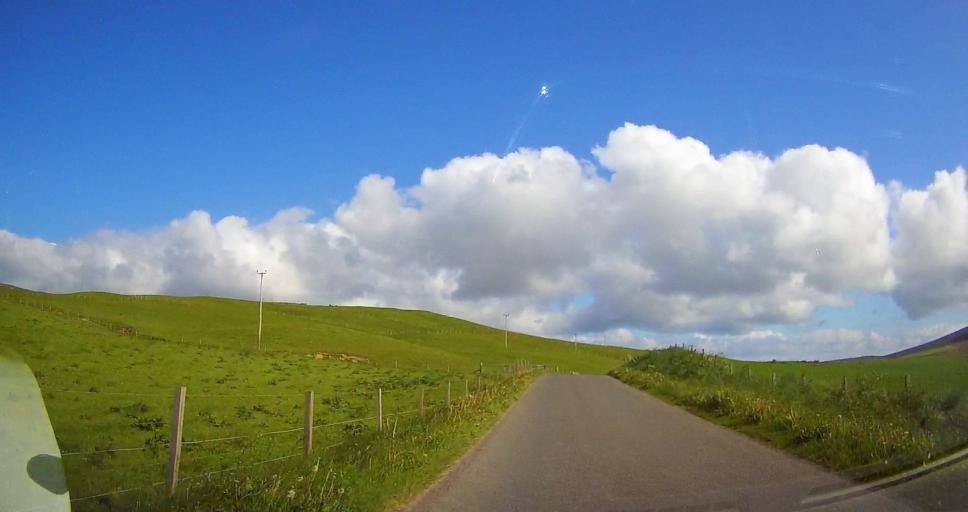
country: GB
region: Scotland
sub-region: Orkney Islands
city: Stromness
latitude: 58.9809
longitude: -3.1378
